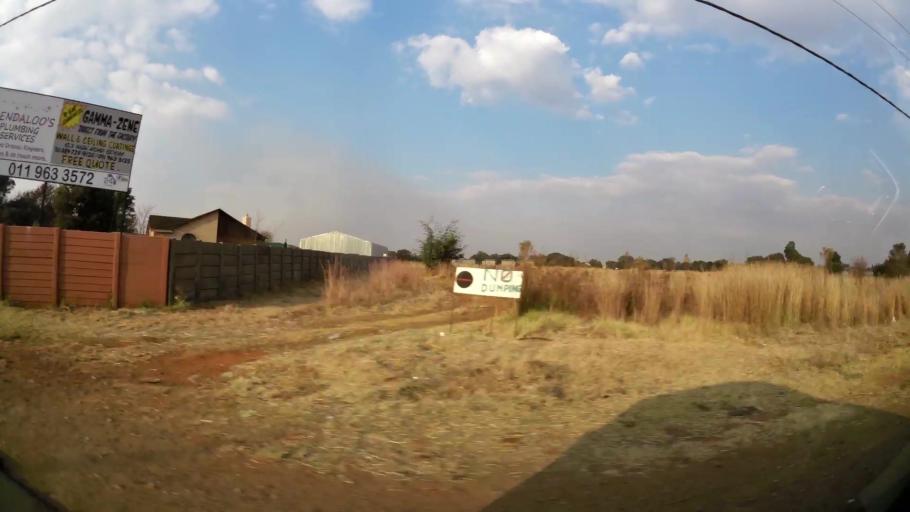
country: ZA
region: Gauteng
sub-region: Ekurhuleni Metropolitan Municipality
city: Benoni
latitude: -26.1279
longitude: 28.2937
